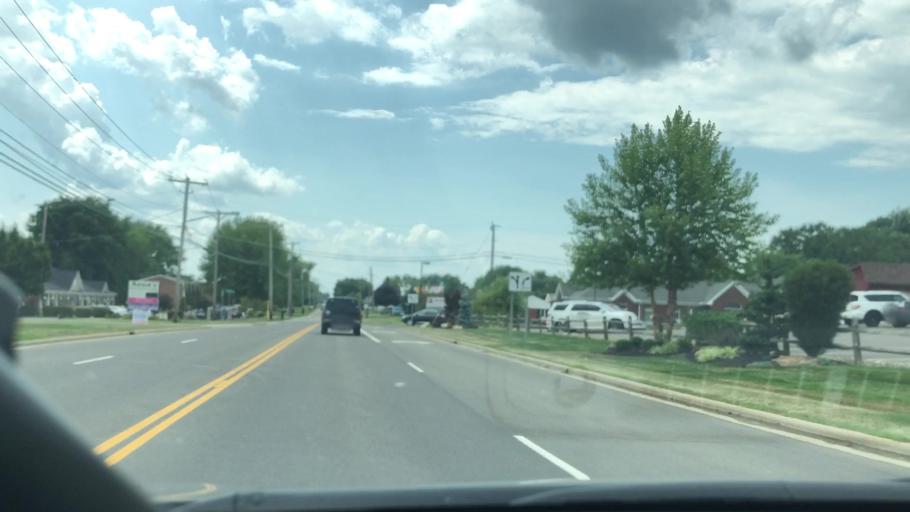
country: US
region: Ohio
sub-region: Summit County
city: Greensburg
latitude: 40.8790
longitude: -81.4831
